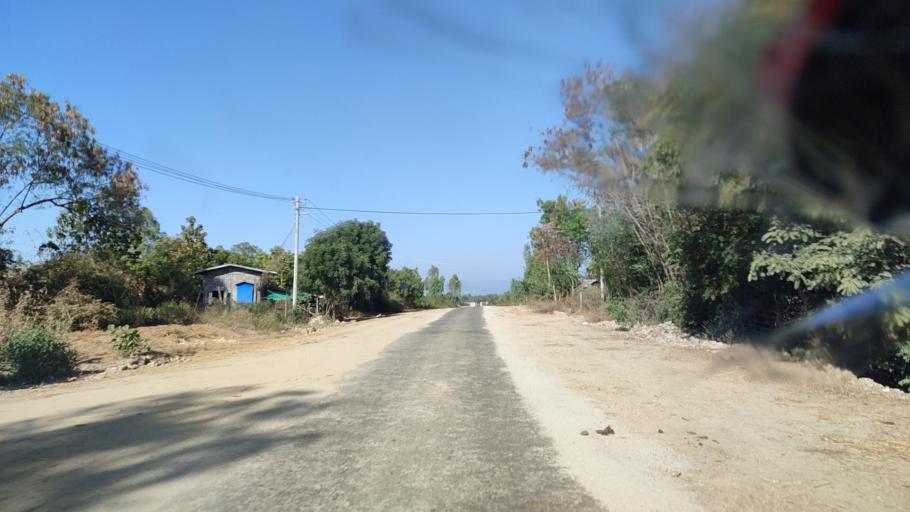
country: MM
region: Mandalay
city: Yamethin
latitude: 20.1096
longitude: 96.2684
